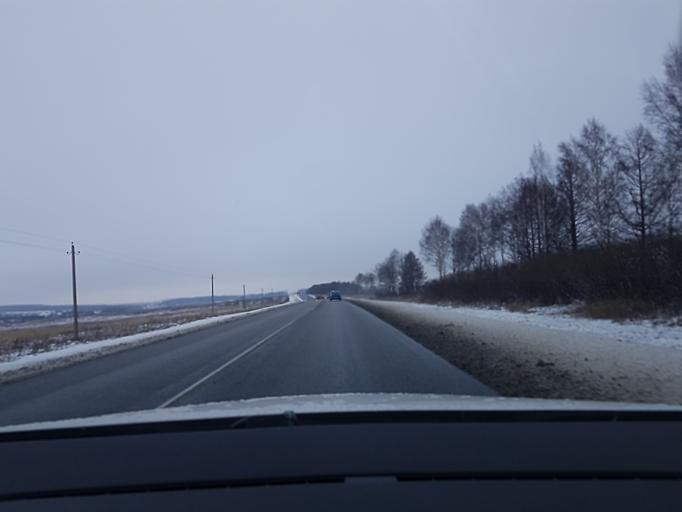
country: RU
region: Moskovskaya
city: Ozherel'ye
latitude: 54.7349
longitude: 38.2572
